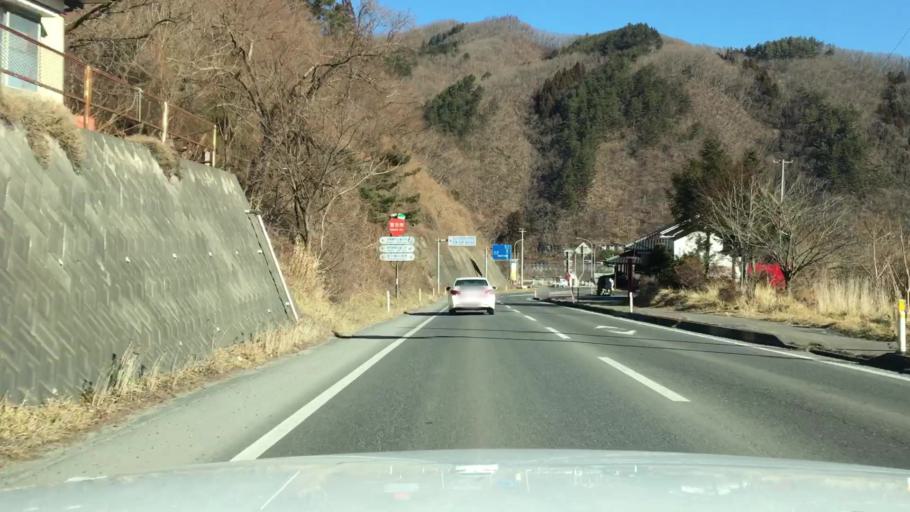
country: JP
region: Iwate
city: Miyako
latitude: 39.6177
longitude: 141.7997
